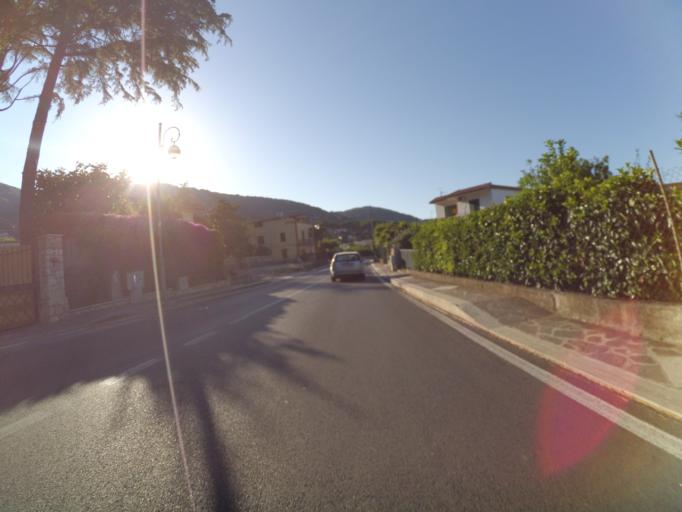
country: IT
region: Latium
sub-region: Provincia di Latina
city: San Felice Circeo
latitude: 41.2354
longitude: 13.0897
